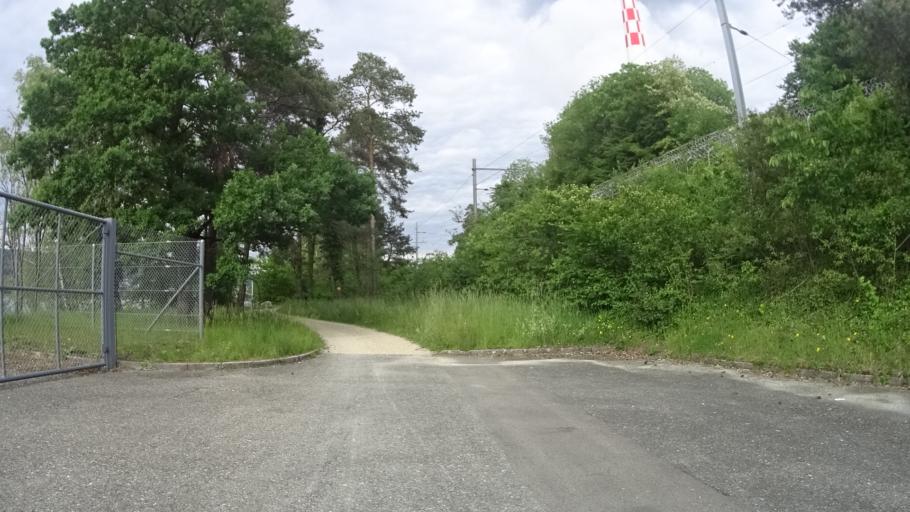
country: CH
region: Aargau
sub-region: Bezirk Zurzach
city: Leibstadt
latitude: 47.6019
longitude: 8.1795
